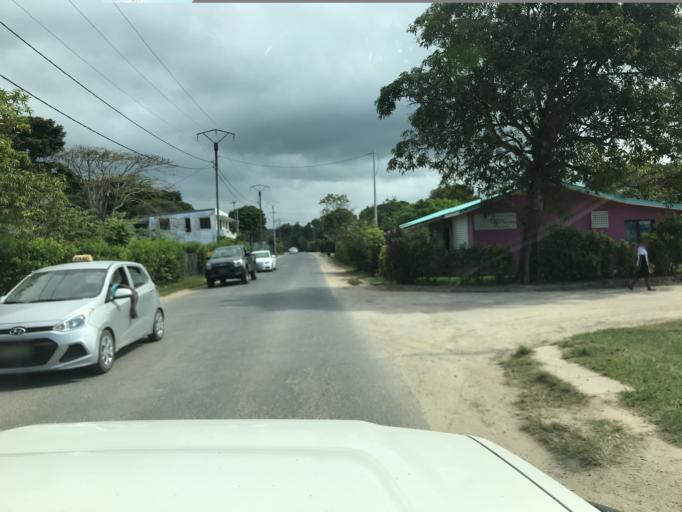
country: VU
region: Sanma
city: Luganville
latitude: -15.5122
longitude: 167.1753
